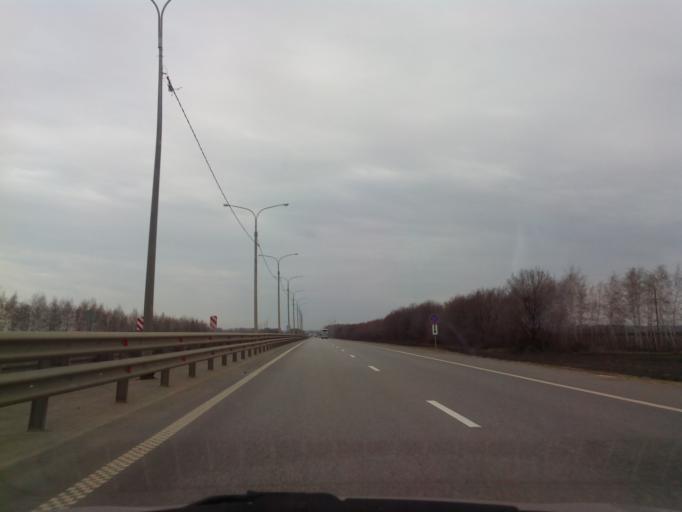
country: RU
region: Tambov
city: Zavoronezhskoye
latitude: 52.8442
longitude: 40.8283
